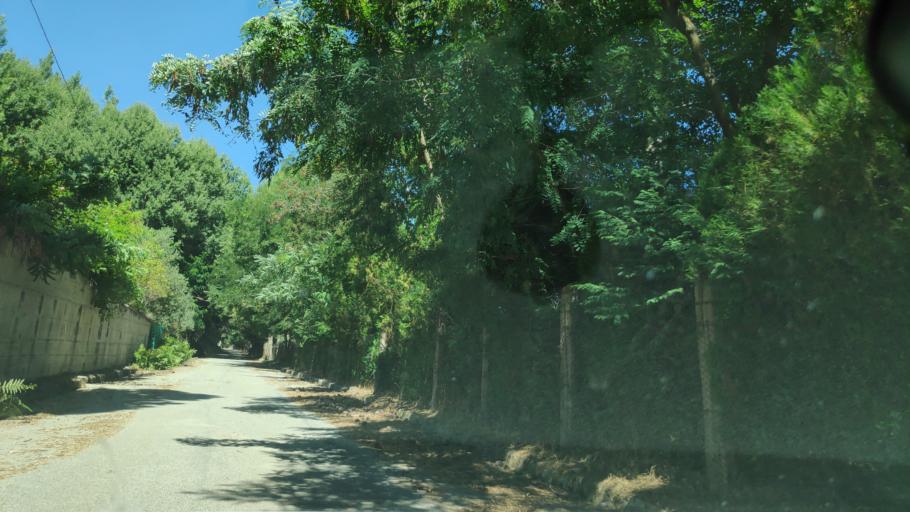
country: IT
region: Calabria
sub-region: Provincia di Reggio Calabria
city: Bova
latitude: 38.0270
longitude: 15.9430
